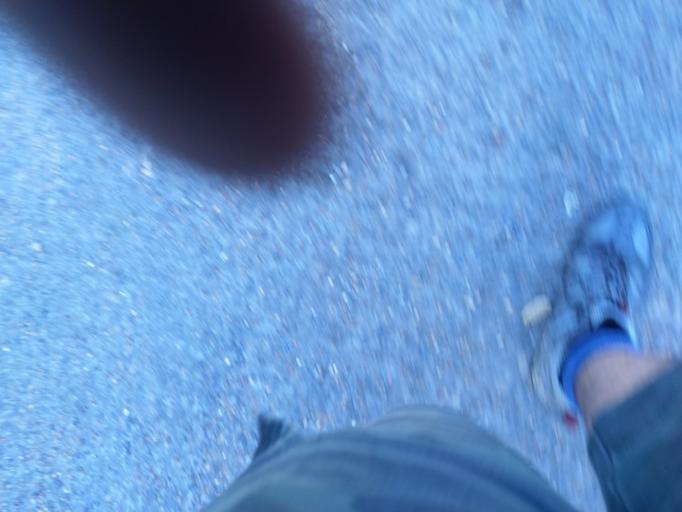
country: NZ
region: Auckland
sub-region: Auckland
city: Pakuranga
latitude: -36.7797
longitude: 174.9920
